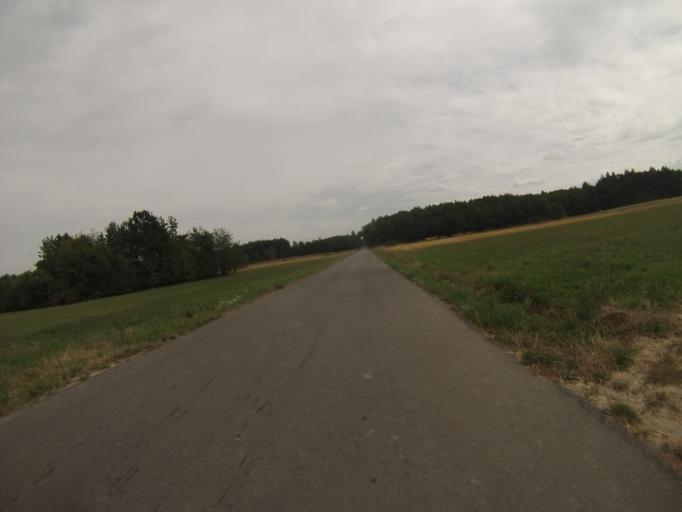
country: PL
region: Swietokrzyskie
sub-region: Powiat kielecki
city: Lagow
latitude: 50.7625
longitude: 21.0709
